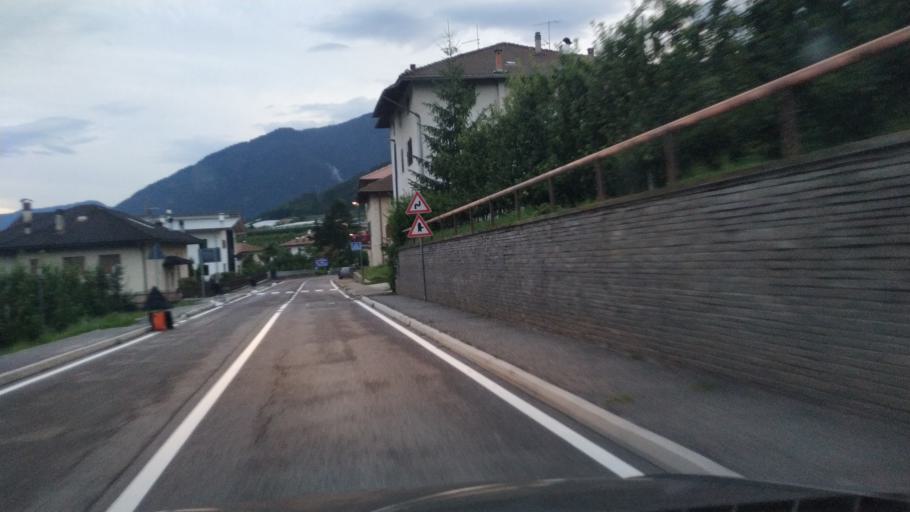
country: IT
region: Trentino-Alto Adige
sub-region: Provincia di Trento
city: Brez
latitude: 46.4308
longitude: 11.1061
